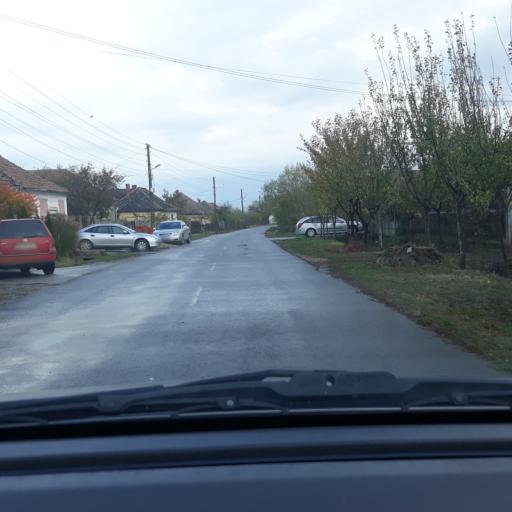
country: RO
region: Bihor
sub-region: Comuna Tarcea
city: Galospetreu
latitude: 47.4865
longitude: 22.2152
